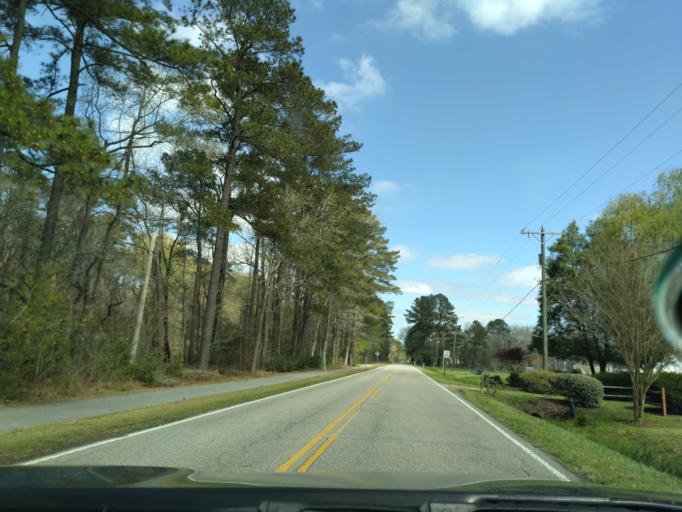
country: US
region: Virginia
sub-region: City of Portsmouth
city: Portsmouth Heights
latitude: 36.6969
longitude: -76.3571
